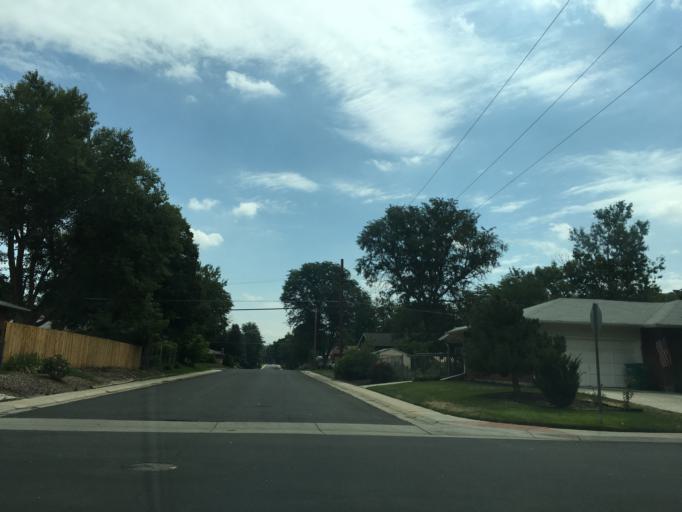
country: US
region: Colorado
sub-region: Arapahoe County
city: Sheridan
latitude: 39.6598
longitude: -105.0513
